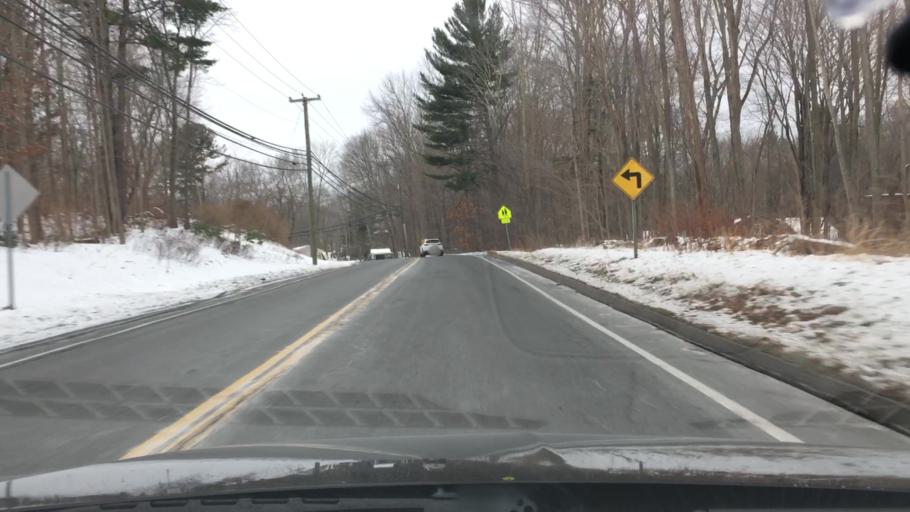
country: US
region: Connecticut
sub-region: Tolland County
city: Tolland
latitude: 41.8511
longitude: -72.3305
